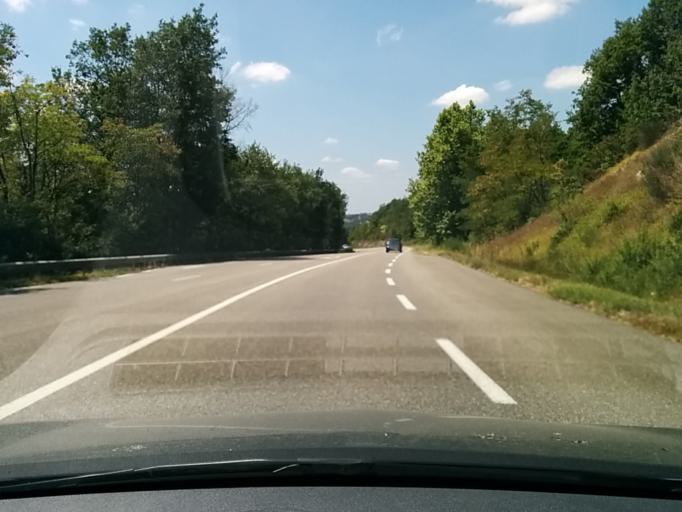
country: FR
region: Midi-Pyrenees
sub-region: Departement du Gers
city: Jegun
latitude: 43.7212
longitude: 0.4055
